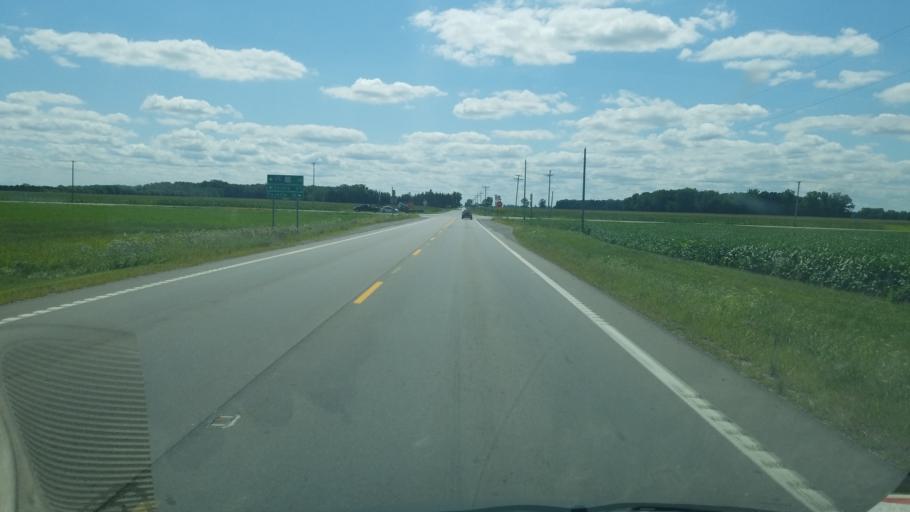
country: US
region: Ohio
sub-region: Fulton County
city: Delta
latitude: 41.6731
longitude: -84.0360
